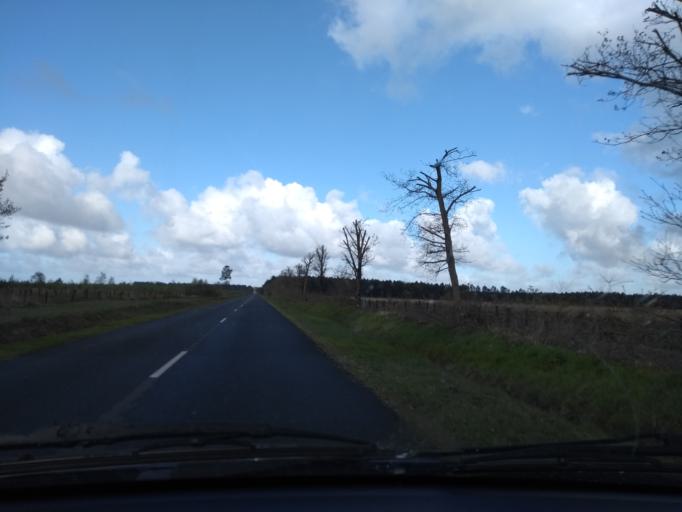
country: FR
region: Aquitaine
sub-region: Departement de la Gironde
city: Mios
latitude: 44.5505
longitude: -0.9618
